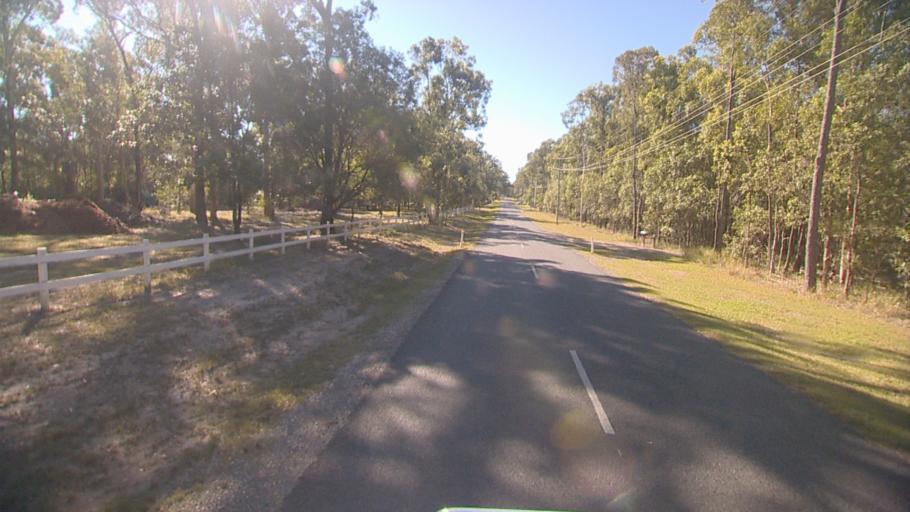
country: AU
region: Queensland
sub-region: Logan
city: Logan Reserve
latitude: -27.7355
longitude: 153.1227
